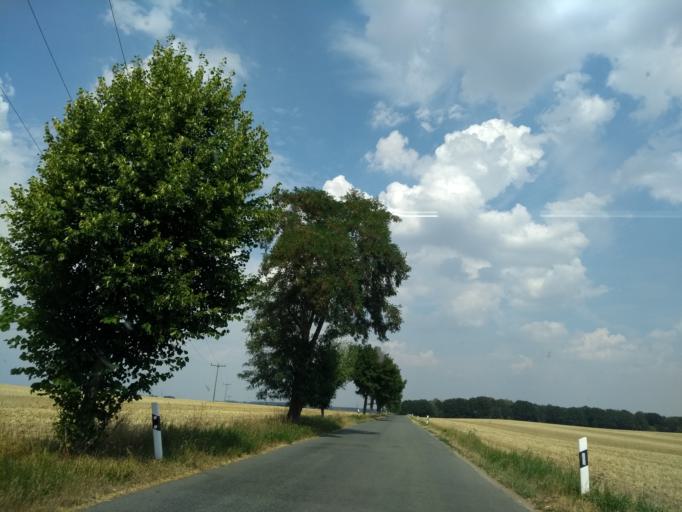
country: DE
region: Thuringia
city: Walpernhain
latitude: 51.0000
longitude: 11.9509
